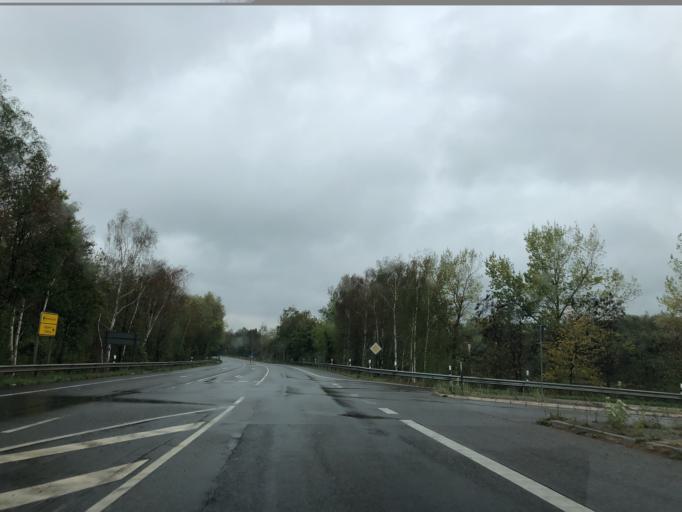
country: DE
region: North Rhine-Westphalia
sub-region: Regierungsbezirk Koln
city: Bedburg
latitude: 51.0380
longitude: 6.5657
